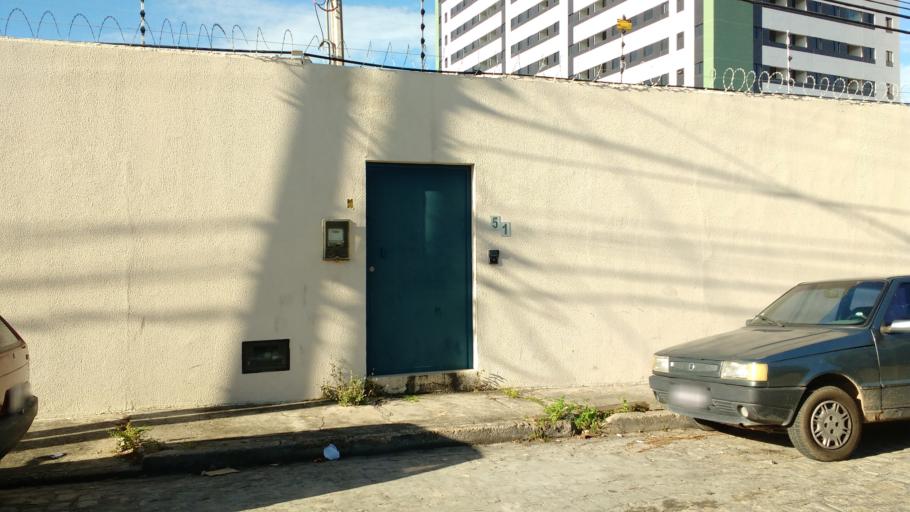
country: BR
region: Alagoas
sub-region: Maceio
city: Maceio
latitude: -9.6338
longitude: -35.7373
